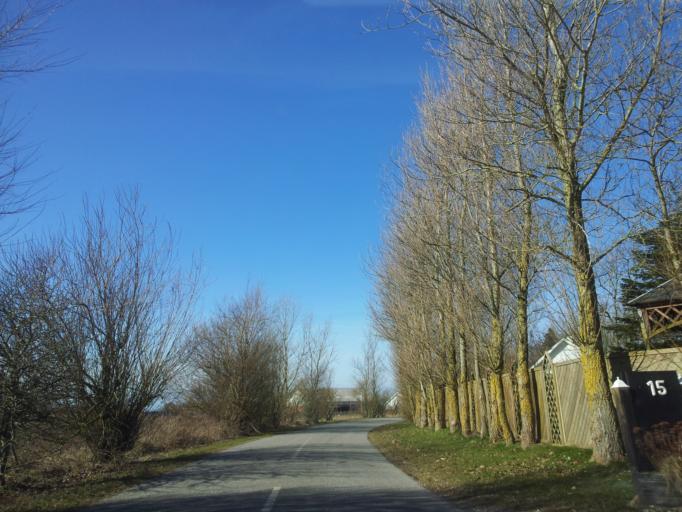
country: DK
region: South Denmark
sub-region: Tonder Kommune
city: Sherrebek
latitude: 55.1811
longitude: 8.7176
